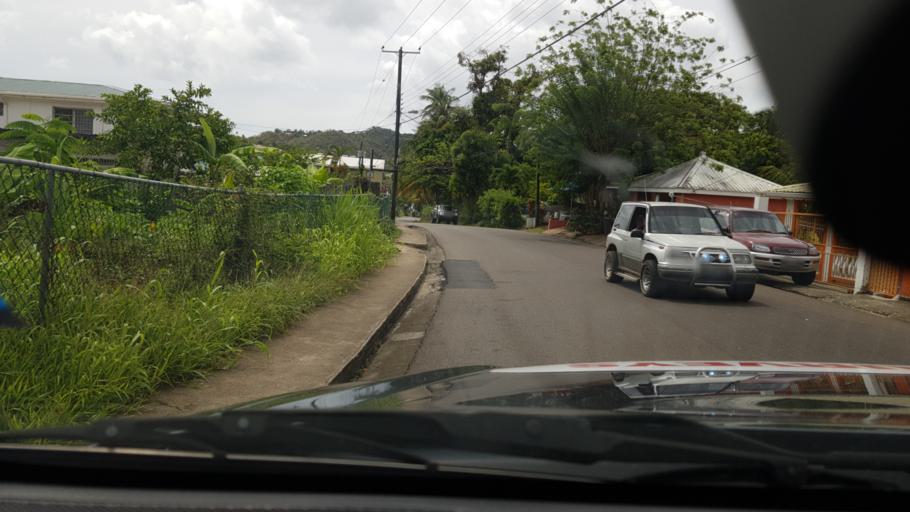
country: LC
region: Castries Quarter
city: Bisee
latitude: 14.0132
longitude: -60.9532
